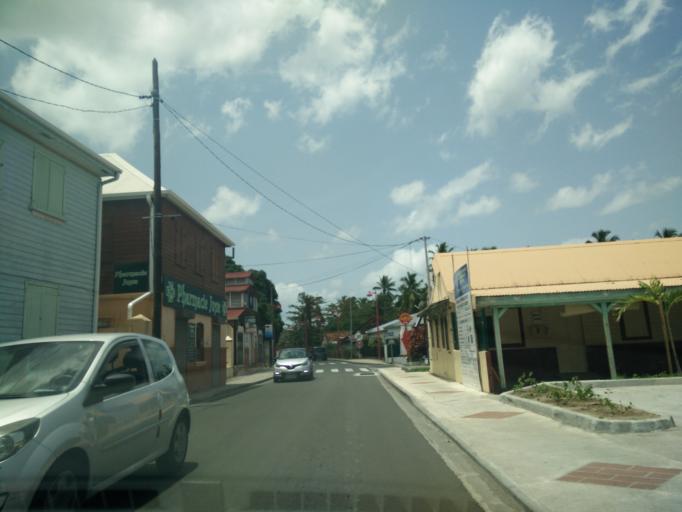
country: MQ
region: Martinique
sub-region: Martinique
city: Saint-Pierre
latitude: 14.7056
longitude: -61.1830
